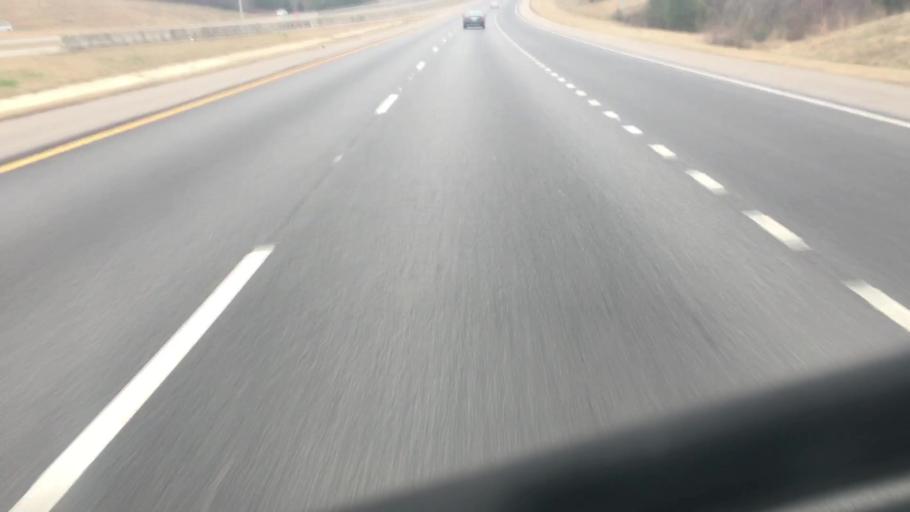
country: US
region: Alabama
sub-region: Jefferson County
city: Fultondale
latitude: 33.5773
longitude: -86.8208
